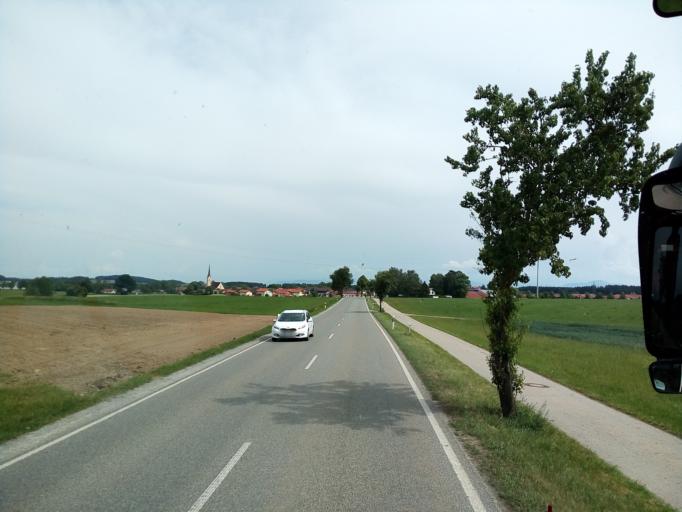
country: DE
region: Bavaria
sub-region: Upper Bavaria
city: Obing
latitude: 48.0062
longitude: 12.3948
